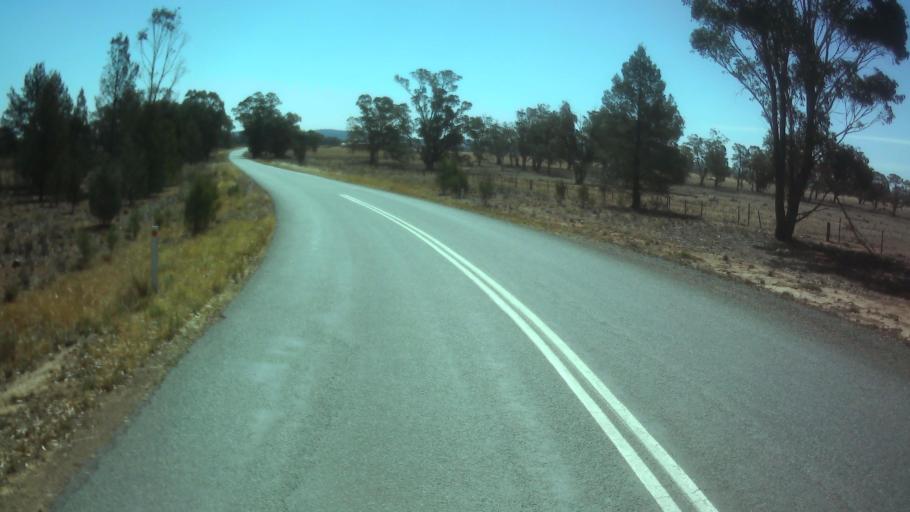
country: AU
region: New South Wales
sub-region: Weddin
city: Grenfell
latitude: -33.8165
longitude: 147.9447
